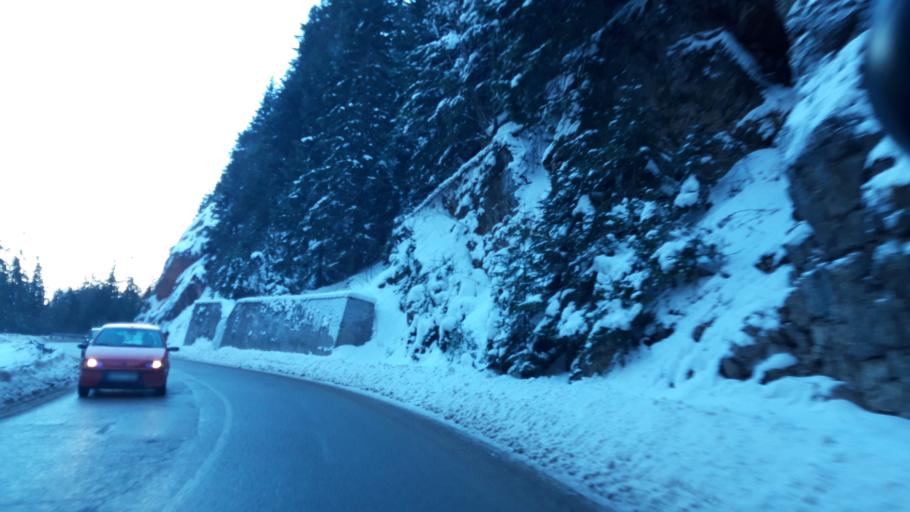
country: BA
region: Republika Srpska
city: Koran
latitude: 43.7664
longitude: 18.5468
